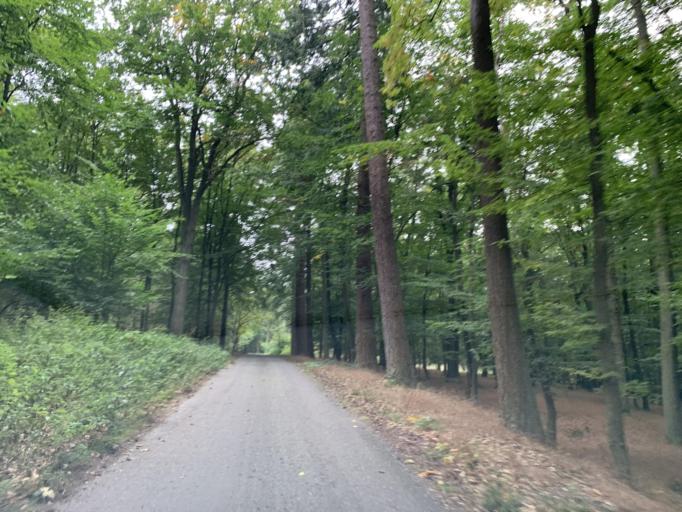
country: DE
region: Mecklenburg-Vorpommern
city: Woldegk
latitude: 53.3209
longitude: 13.6092
